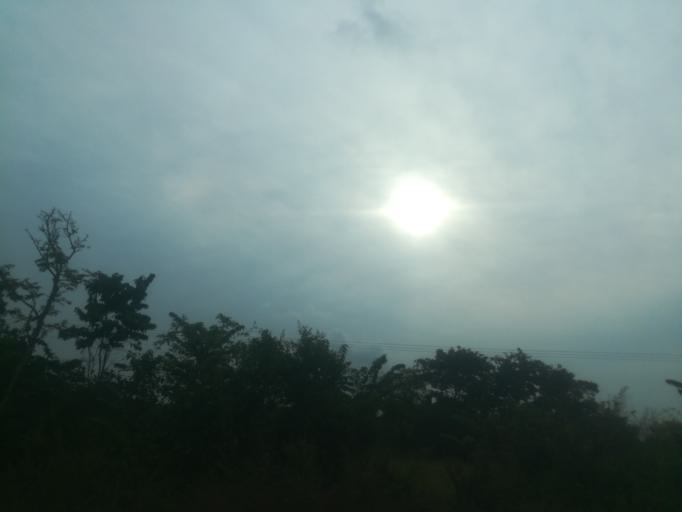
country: NG
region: Ogun
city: Ayetoro
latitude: 7.2343
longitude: 3.1346
